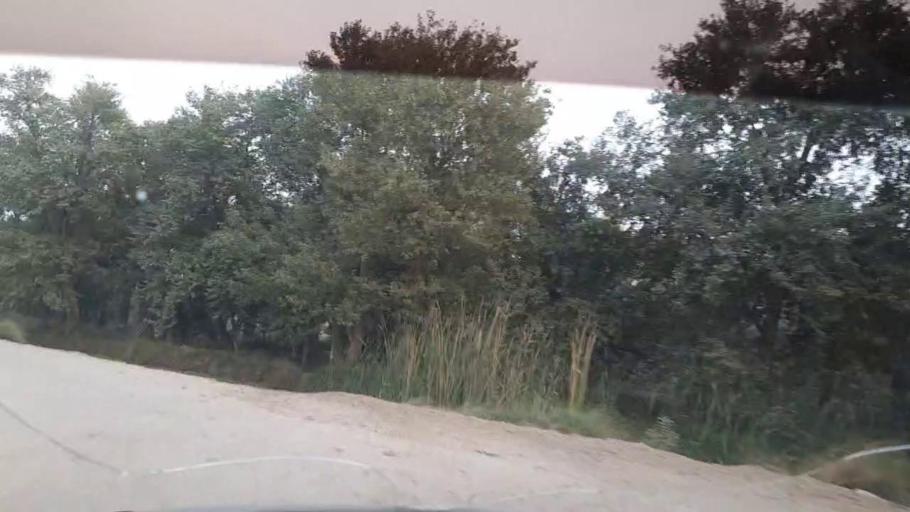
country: PK
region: Sindh
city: Khairpur
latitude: 27.5732
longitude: 68.7260
